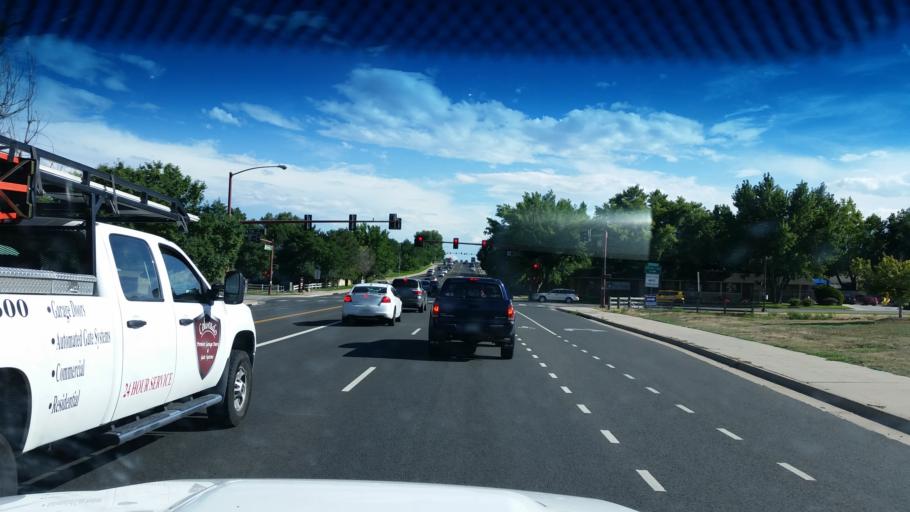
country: US
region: Colorado
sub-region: Adams County
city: Northglenn
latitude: 39.9218
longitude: -104.9404
